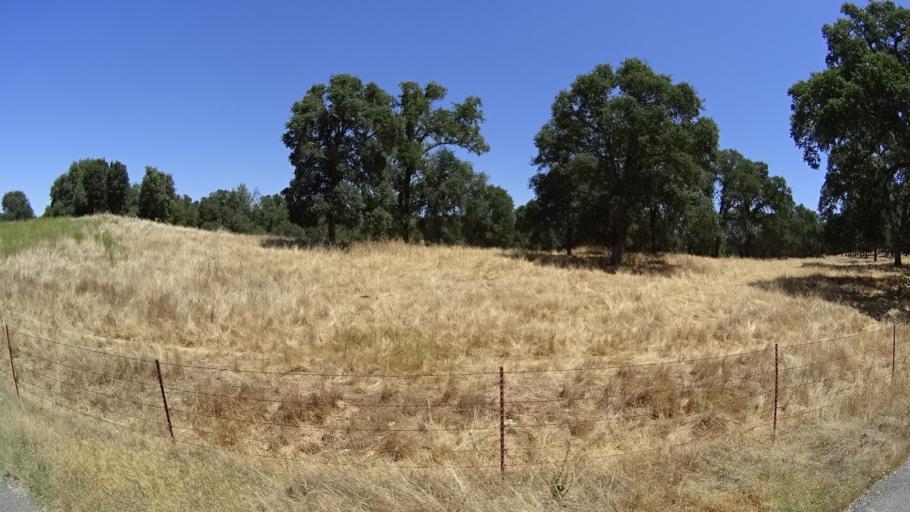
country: US
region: California
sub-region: Calaveras County
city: Angels Camp
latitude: 38.1103
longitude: -120.6121
